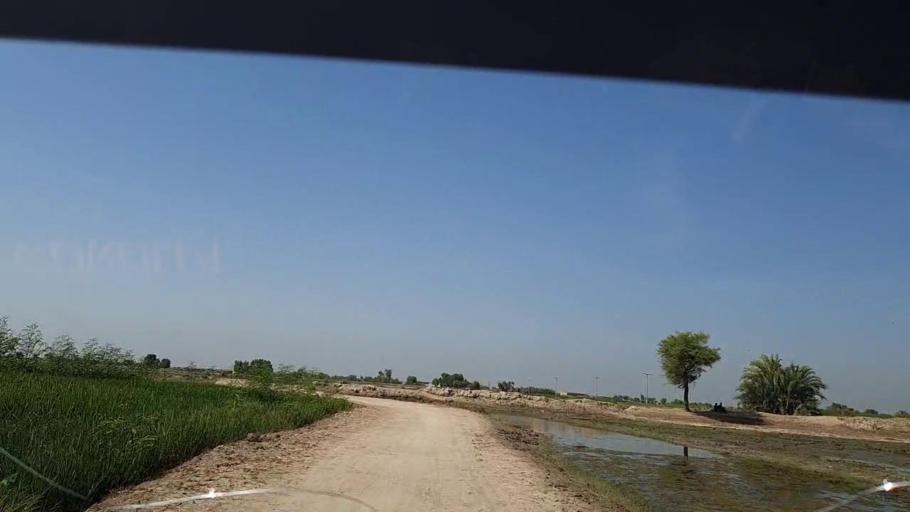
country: PK
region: Sindh
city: Tangwani
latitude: 28.3247
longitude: 69.0865
